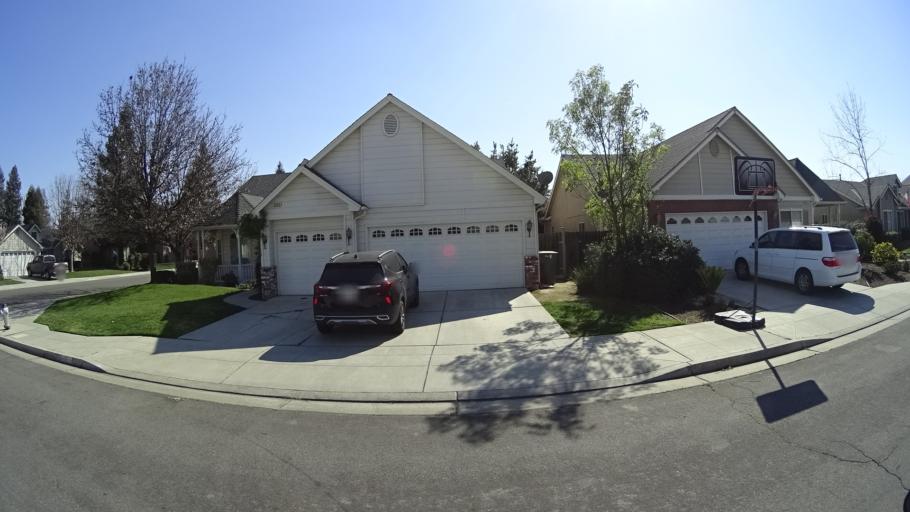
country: US
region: California
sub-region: Fresno County
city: Clovis
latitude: 36.8700
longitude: -119.7310
